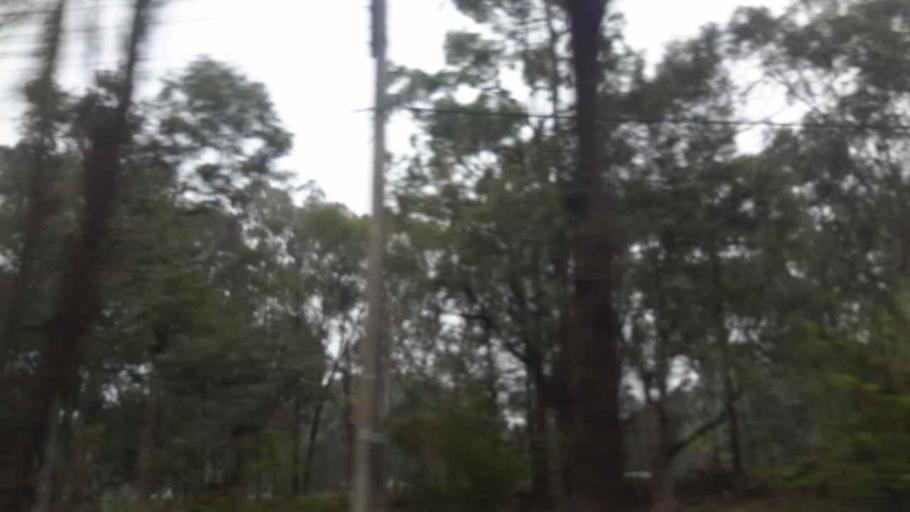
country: AU
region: New South Wales
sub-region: Hawkesbury
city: Richmond
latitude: -33.6680
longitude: 150.7550
